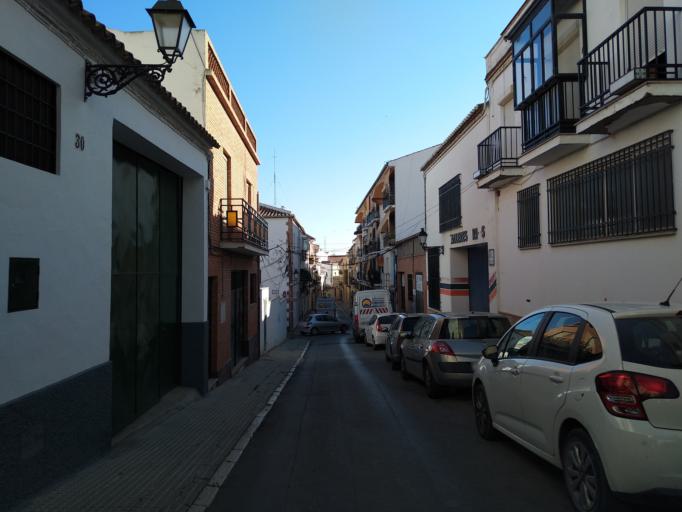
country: ES
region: Andalusia
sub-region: Provincia de Malaga
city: Antequera
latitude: 37.0171
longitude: -4.5633
